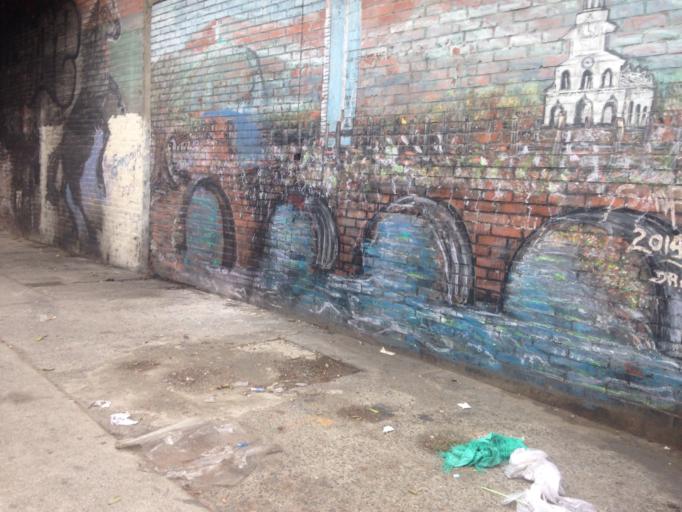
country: CO
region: Valle del Cauca
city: Cali
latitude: 3.4514
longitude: -76.5232
